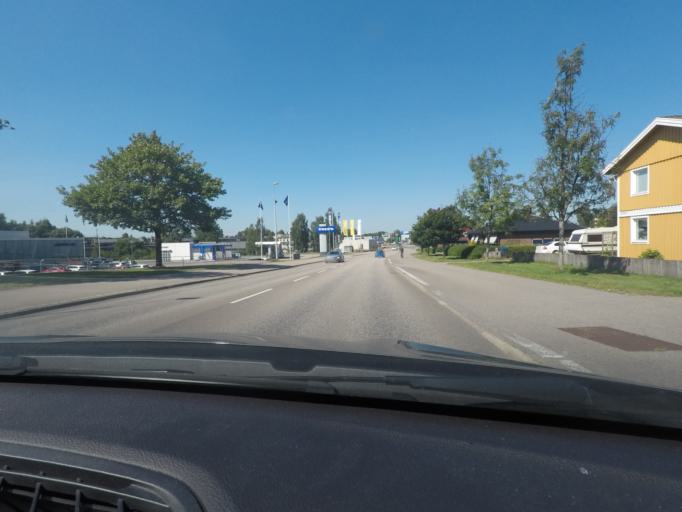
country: SE
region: Kronoberg
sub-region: Markaryds Kommun
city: Markaryd
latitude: 56.4547
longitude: 13.5948
